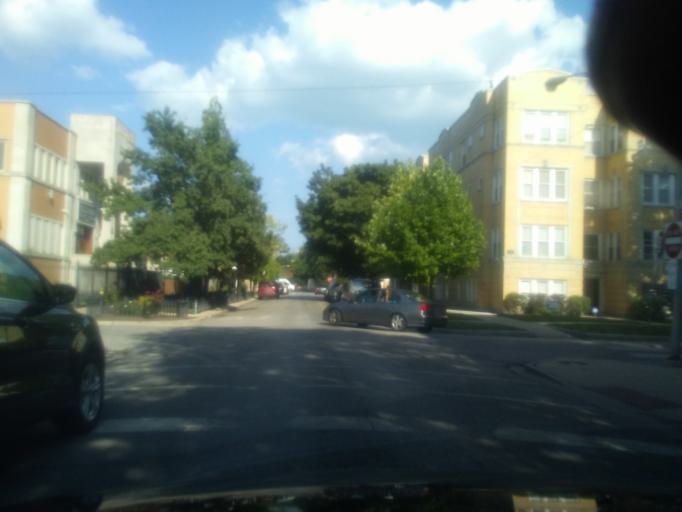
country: US
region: Illinois
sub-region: Cook County
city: Lincolnwood
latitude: 41.9702
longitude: -87.7149
